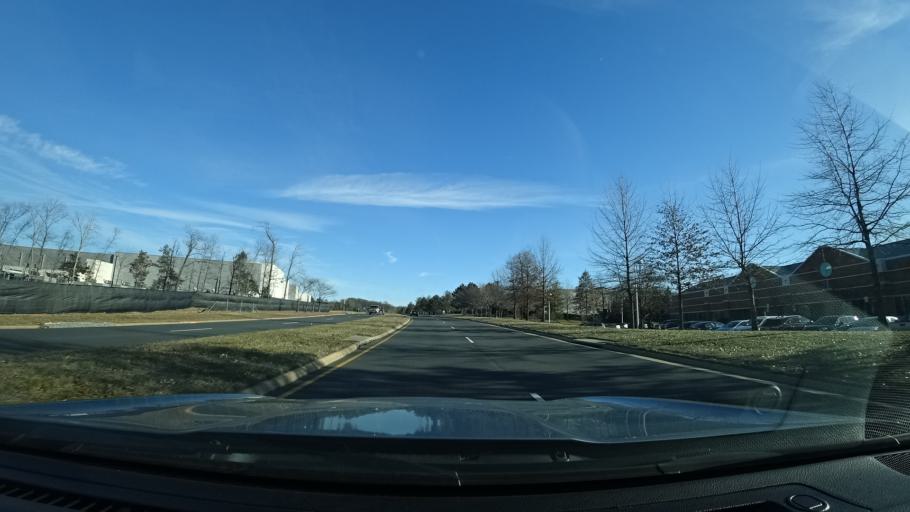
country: US
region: Virginia
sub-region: Loudoun County
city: Dulles Town Center
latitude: 39.0253
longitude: -77.4172
